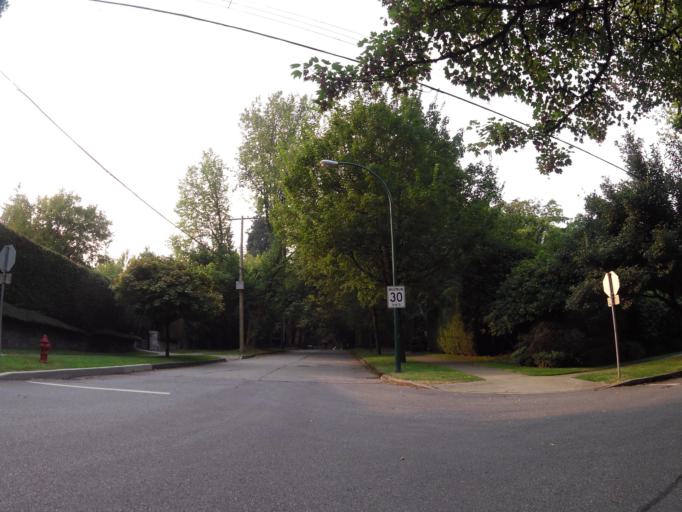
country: CA
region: British Columbia
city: Vancouver
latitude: 49.2530
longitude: -123.1486
